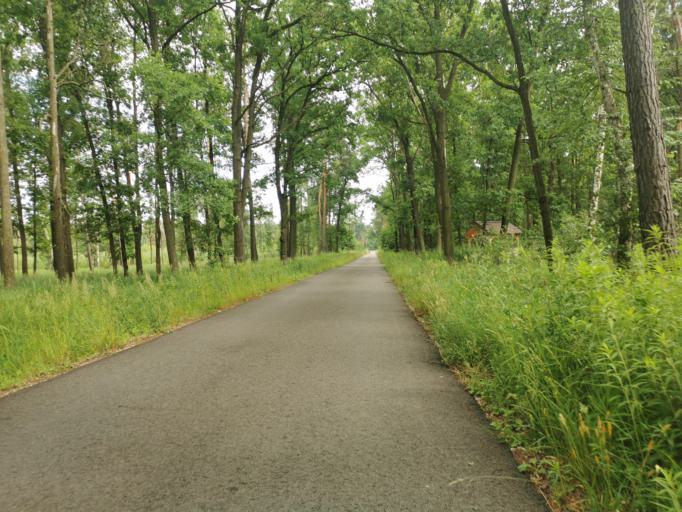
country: SK
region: Trnavsky
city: Gbely
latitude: 48.7382
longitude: 17.0881
